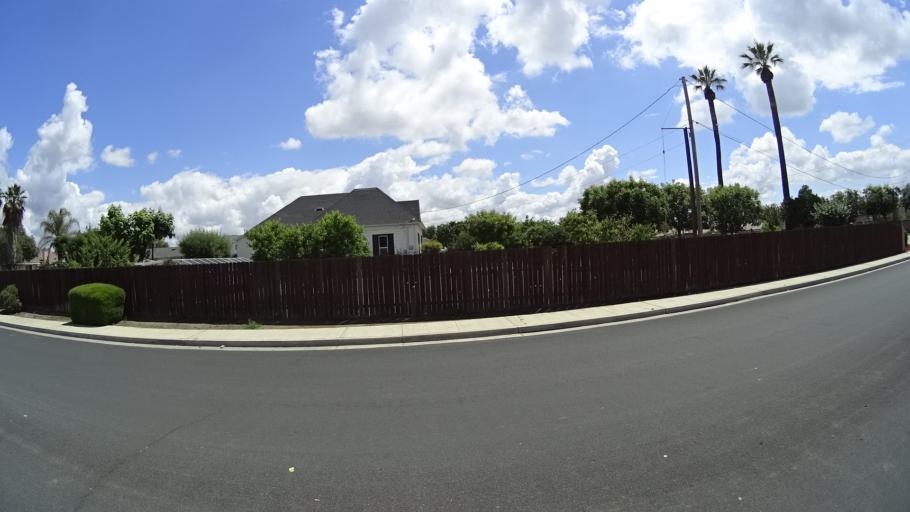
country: US
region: California
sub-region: Kings County
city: Lucerne
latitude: 36.3576
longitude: -119.6619
